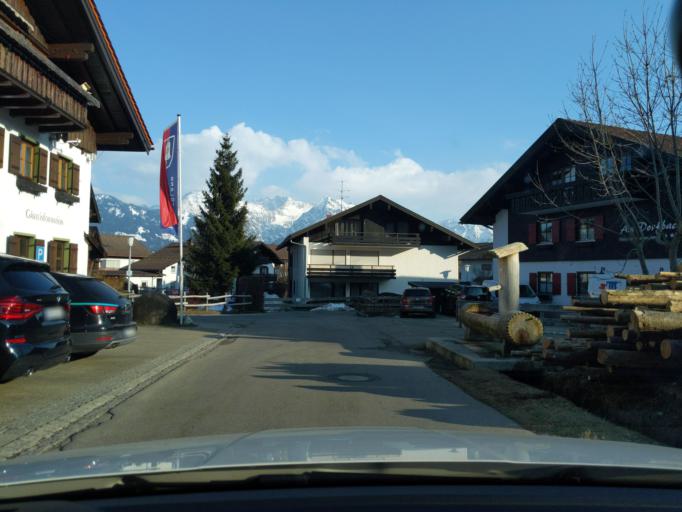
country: DE
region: Bavaria
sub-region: Swabia
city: Bolsterlang
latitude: 47.4597
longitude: 10.2335
